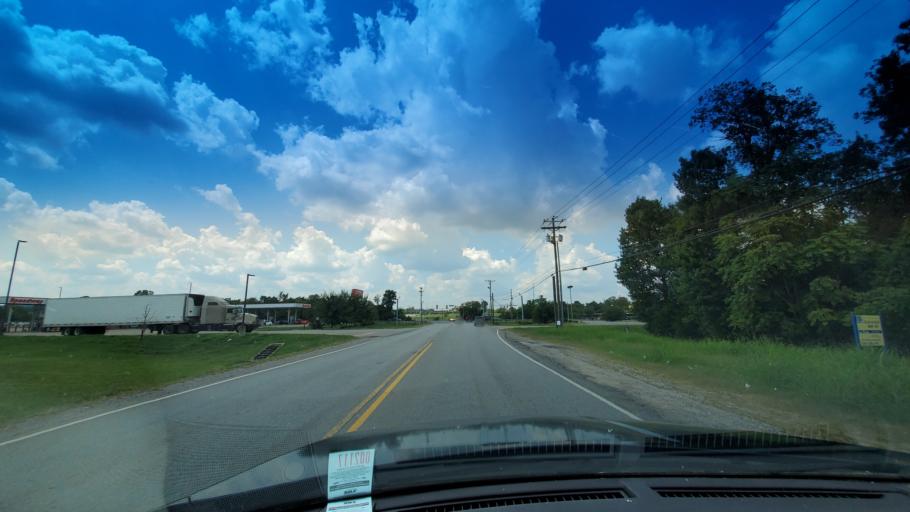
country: US
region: Tennessee
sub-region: Wilson County
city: Lebanon
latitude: 36.1737
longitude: -86.3008
